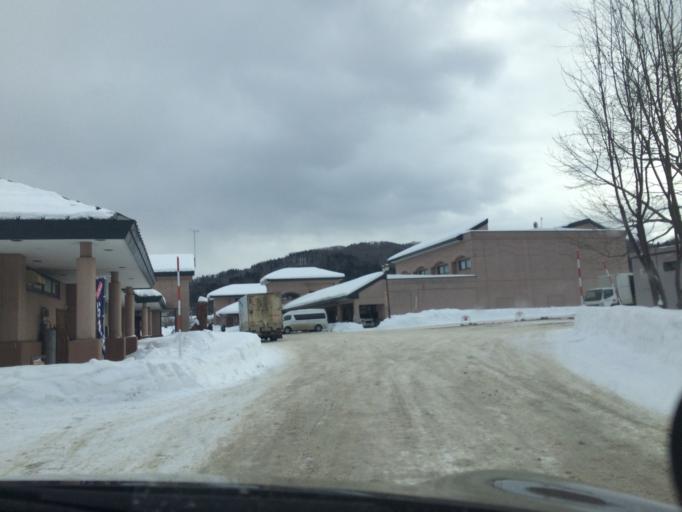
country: JP
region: Hokkaido
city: Shimo-furano
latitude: 42.9791
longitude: 142.3971
